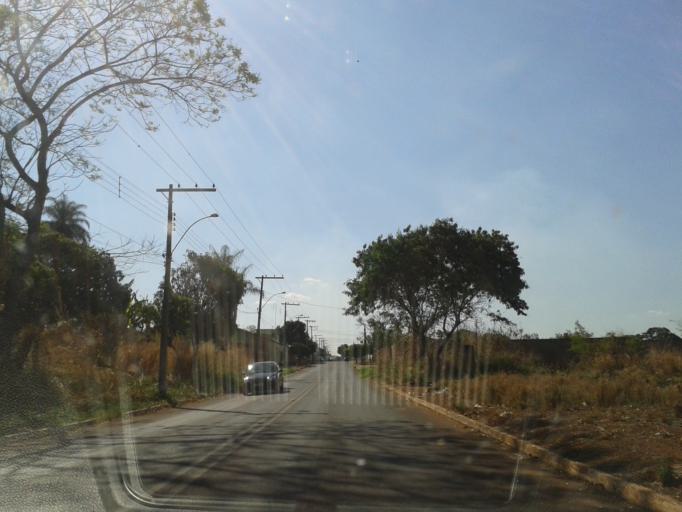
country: BR
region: Minas Gerais
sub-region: Araguari
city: Araguari
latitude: -18.6587
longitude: -48.1788
